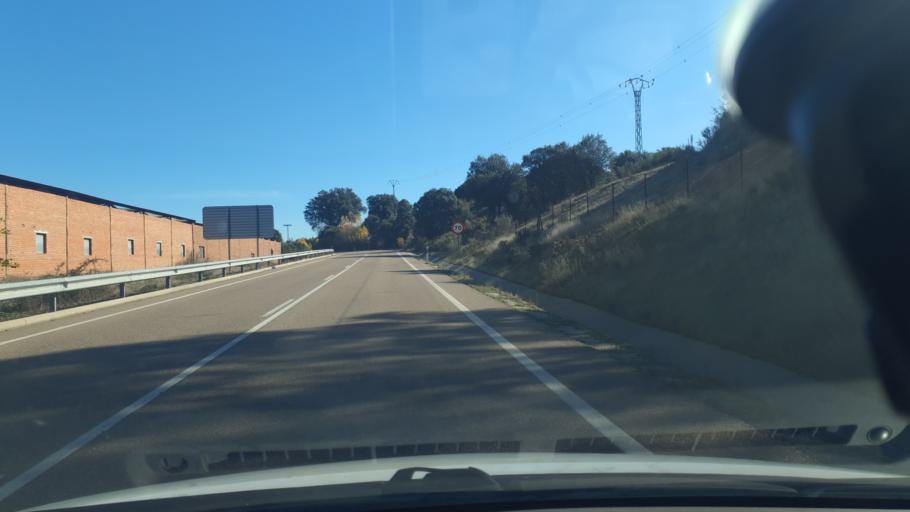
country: ES
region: Castille and Leon
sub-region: Provincia de Avila
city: Arenas de San Pedro
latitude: 40.1790
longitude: -5.0440
